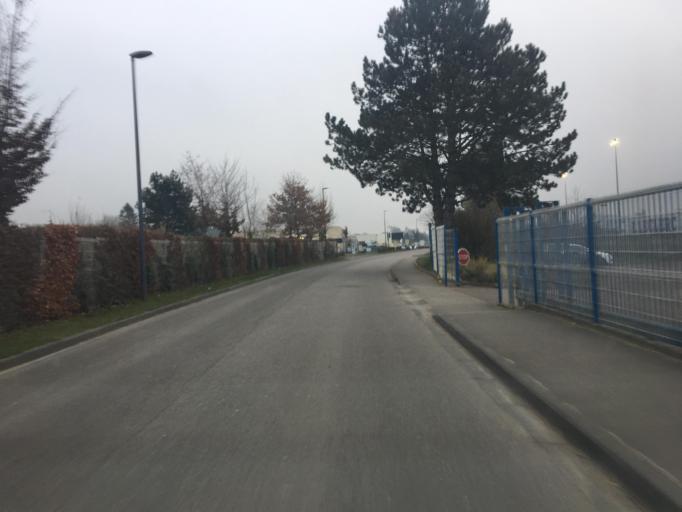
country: FR
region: Haute-Normandie
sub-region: Departement de la Seine-Maritime
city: Neufchatel-en-Bray
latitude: 49.7357
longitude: 1.4324
